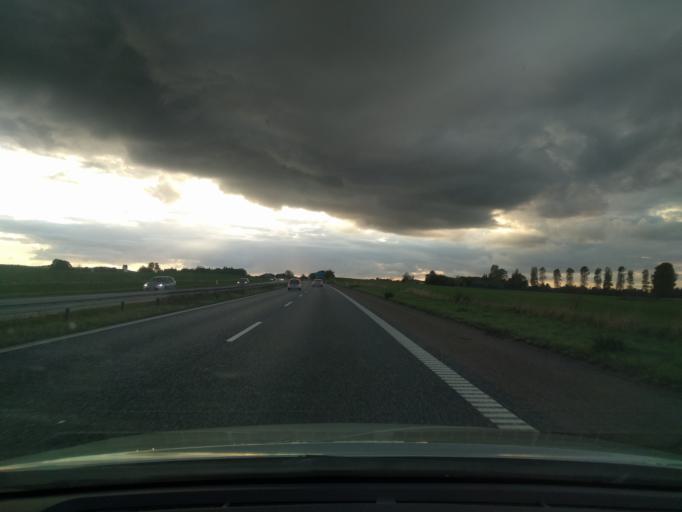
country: DK
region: Zealand
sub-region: Slagelse Kommune
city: Slagelse
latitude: 55.4278
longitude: 11.4369
